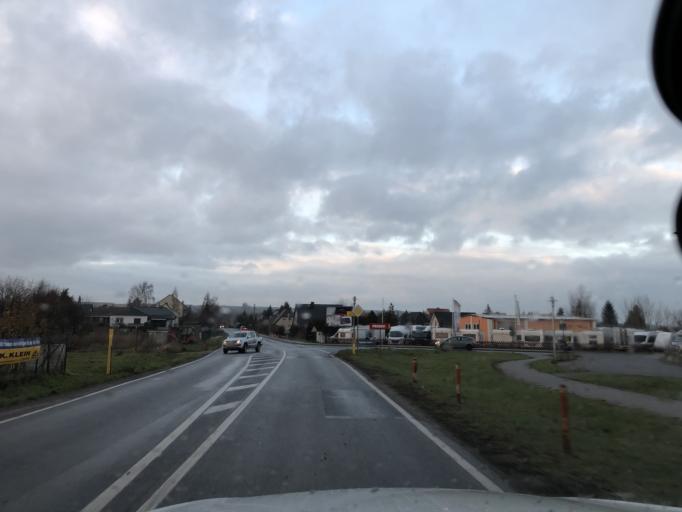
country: DE
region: Saxony-Anhalt
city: Langenbogen
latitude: 51.4797
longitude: 11.7799
